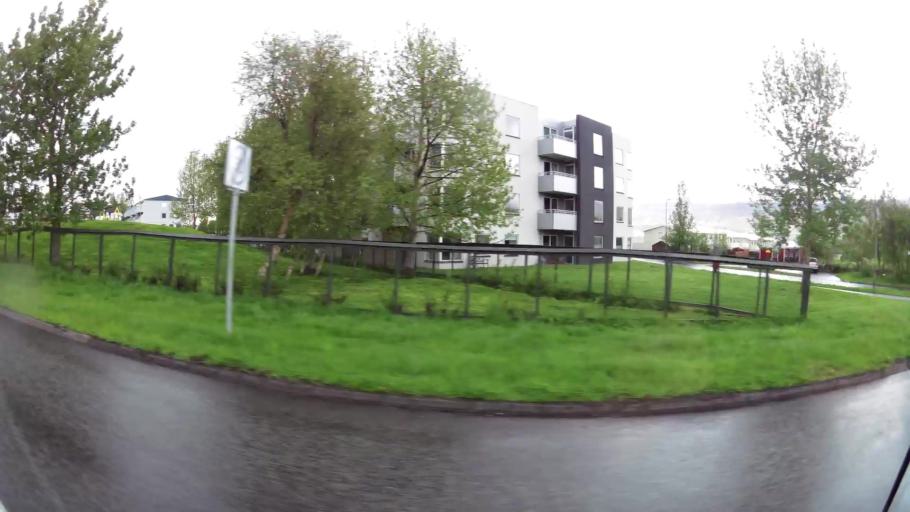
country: IS
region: Northeast
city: Akureyri
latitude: 65.6890
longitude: -18.1357
